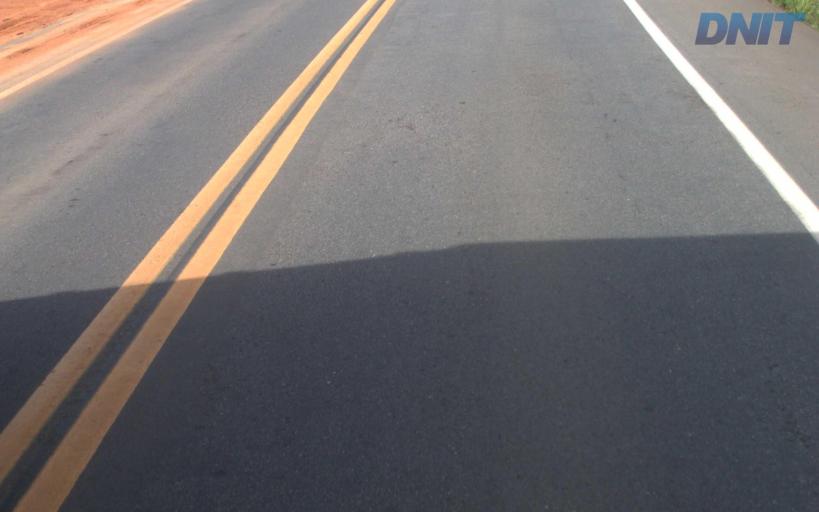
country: BR
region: Minas Gerais
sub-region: Belo Oriente
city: Belo Oriente
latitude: -19.2445
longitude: -42.3369
